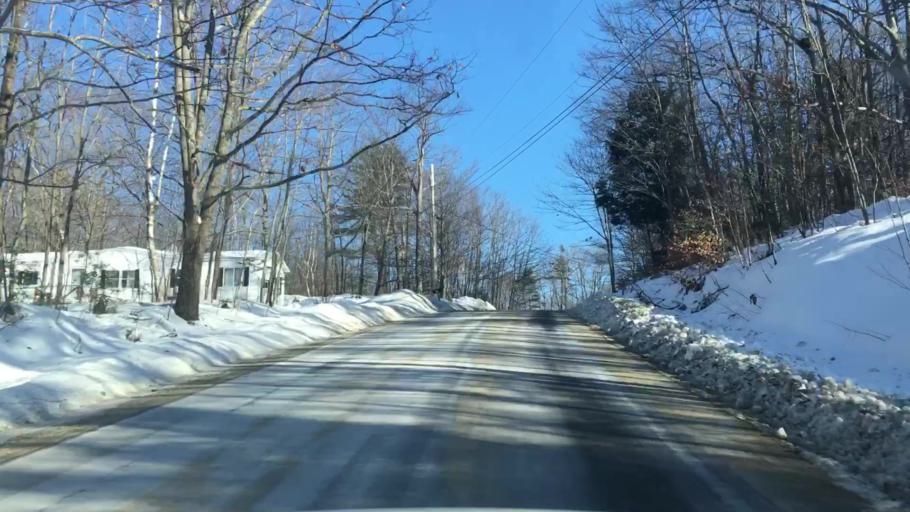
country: US
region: Maine
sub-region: Oxford County
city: Paris
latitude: 44.2693
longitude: -70.4500
